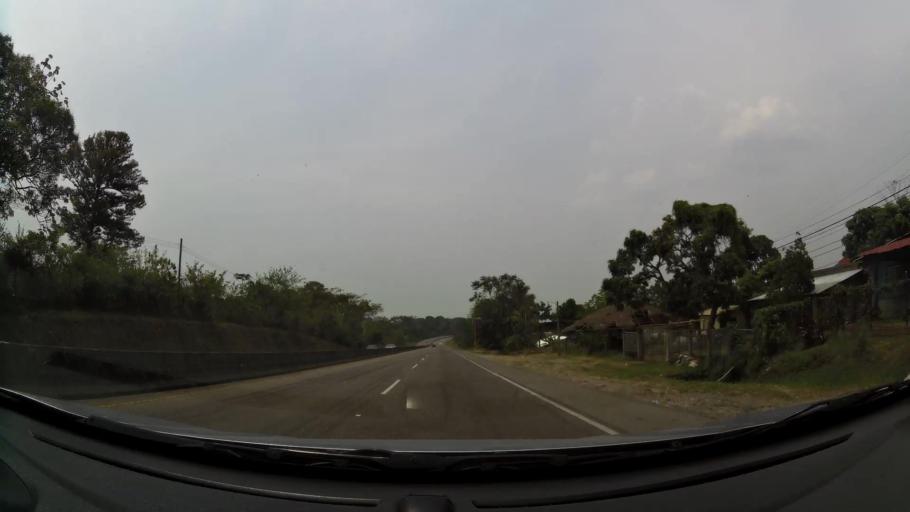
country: HN
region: Cortes
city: Oropendolas
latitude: 14.9960
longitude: -87.9312
